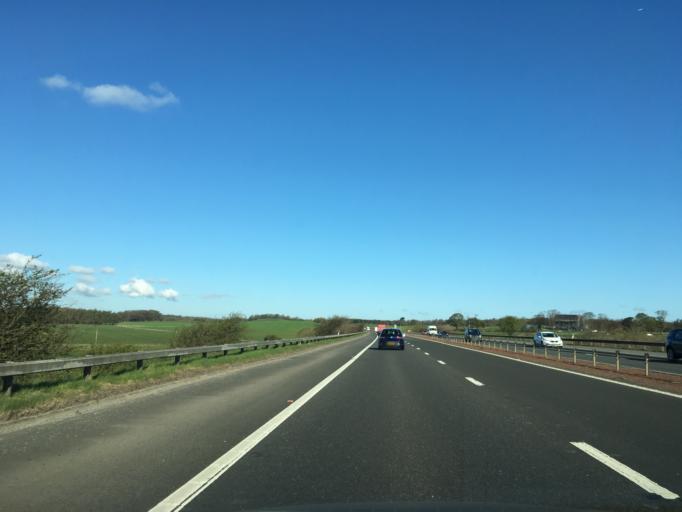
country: GB
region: Scotland
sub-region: West Lothian
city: Broxburn
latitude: 55.9684
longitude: -3.4527
